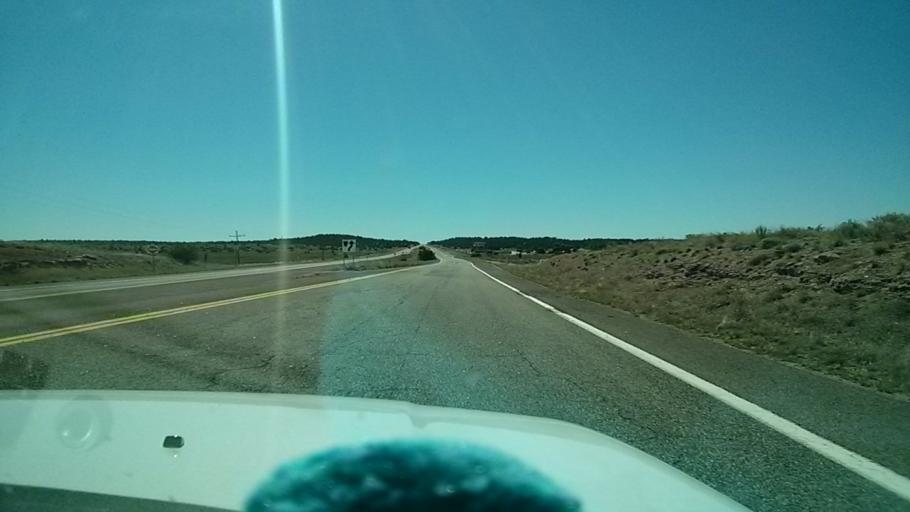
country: US
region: Arizona
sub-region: Mohave County
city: Peach Springs
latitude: 35.5320
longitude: -113.2383
